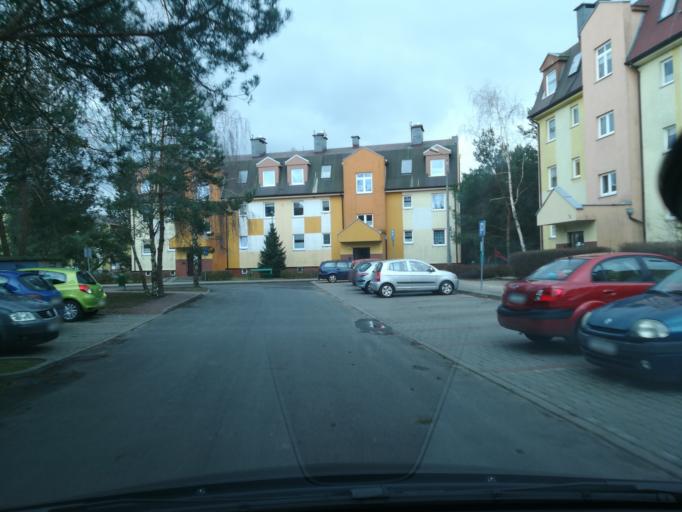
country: PL
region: Kujawsko-Pomorskie
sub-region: Powiat torunski
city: Lubicz Dolny
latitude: 52.9829
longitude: 18.6825
